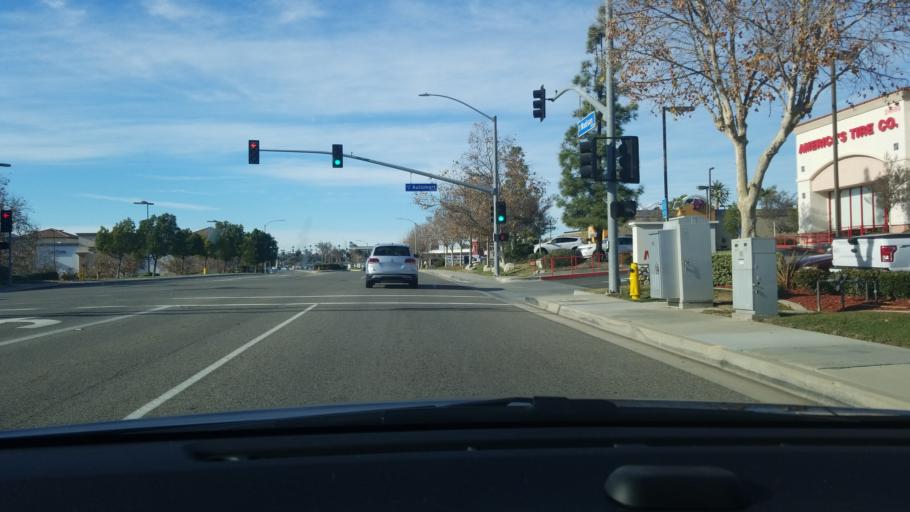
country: US
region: California
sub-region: Riverside County
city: Murrieta
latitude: 33.5623
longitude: -117.2056
